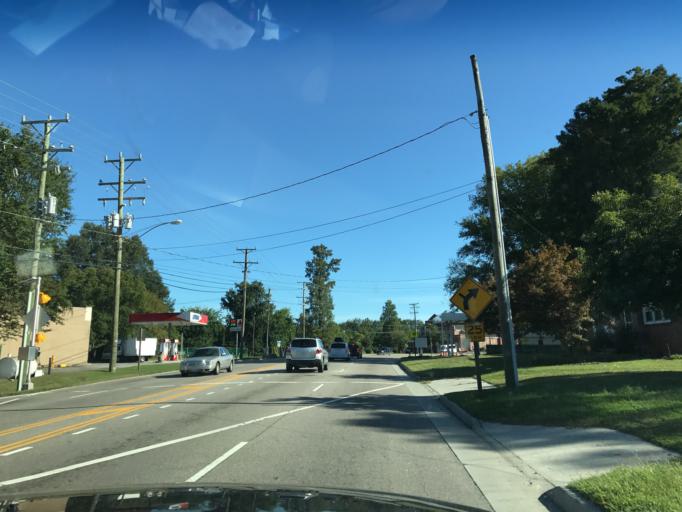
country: US
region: Virginia
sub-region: City of Portsmouth
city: Portsmouth Heights
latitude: 36.7448
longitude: -76.3456
